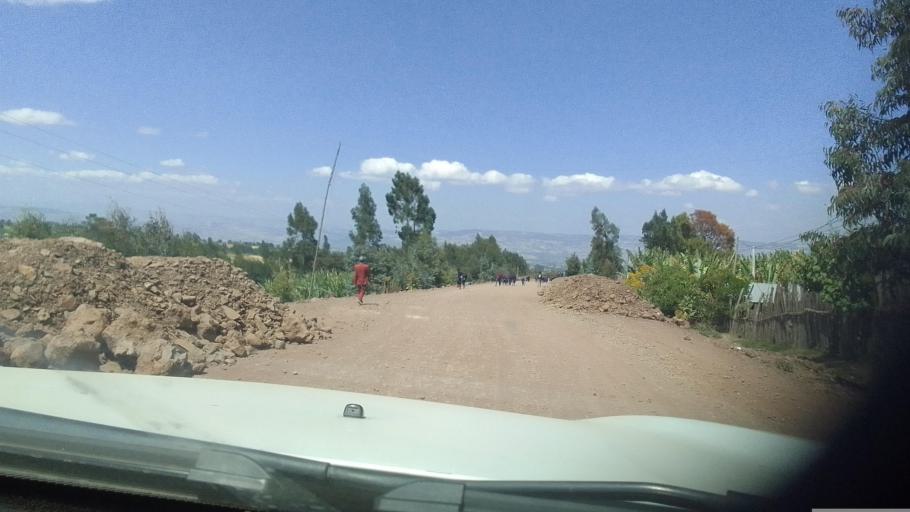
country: ET
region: Oromiya
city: Hagere Hiywet
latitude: 8.8583
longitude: 37.8916
